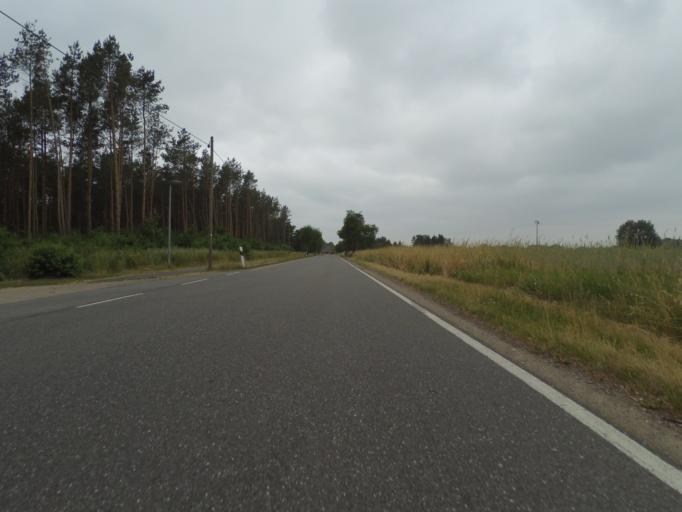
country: DE
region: Mecklenburg-Vorpommern
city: Spornitz
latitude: 53.4803
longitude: 11.6676
